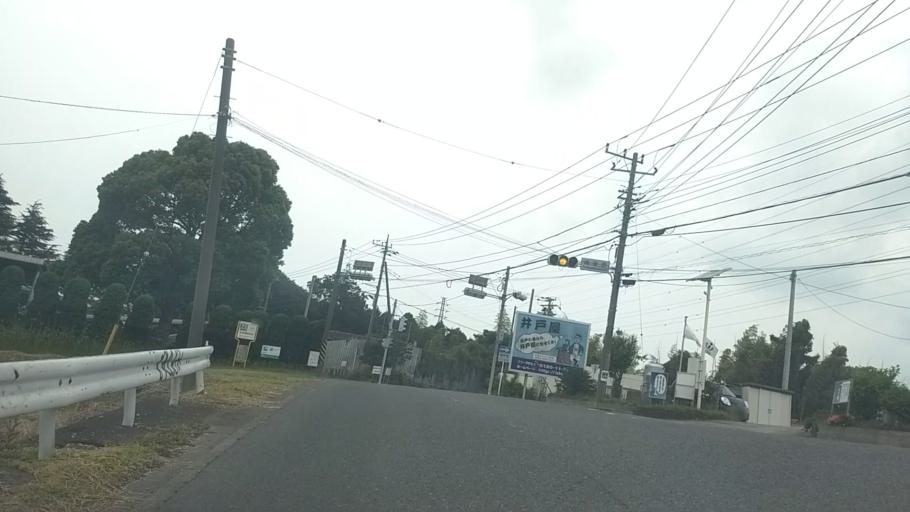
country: JP
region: Kanagawa
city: Fujisawa
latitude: 35.3607
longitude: 139.4343
